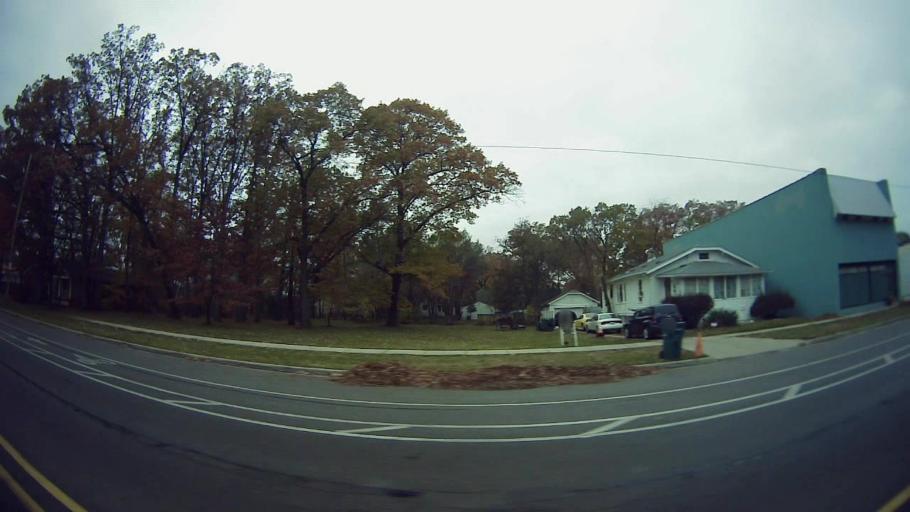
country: US
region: Michigan
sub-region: Oakland County
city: Ferndale
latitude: 42.4476
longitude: -83.1422
